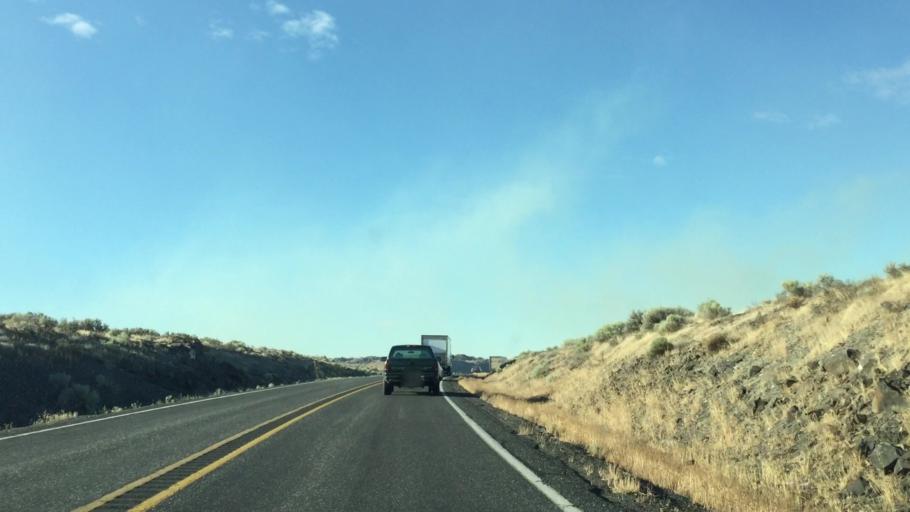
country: US
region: Washington
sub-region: Grant County
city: Mattawa
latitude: 46.9128
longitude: -119.9466
